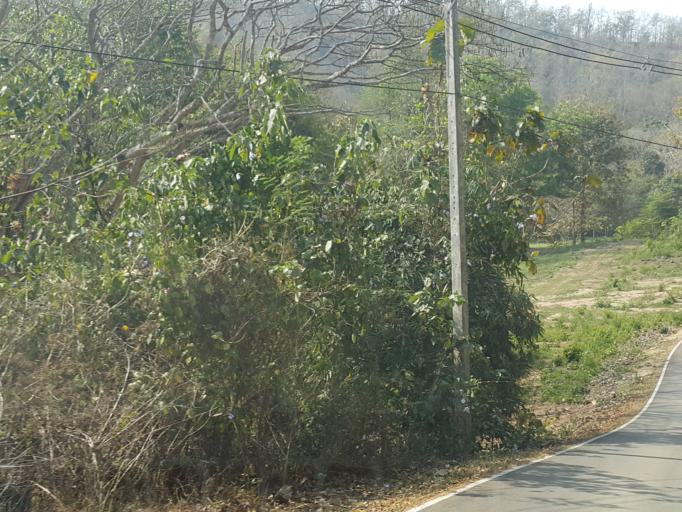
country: TH
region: Chiang Mai
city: Hang Dong
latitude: 18.7209
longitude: 98.8309
